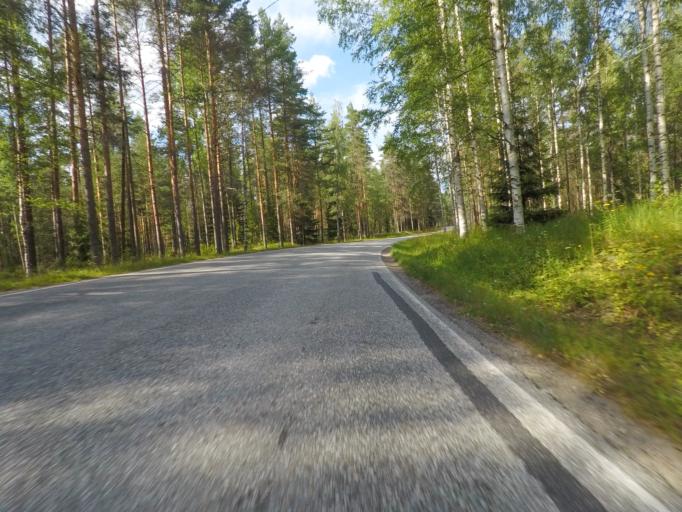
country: FI
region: Southern Savonia
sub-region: Mikkeli
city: Puumala
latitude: 61.7007
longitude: 28.2104
